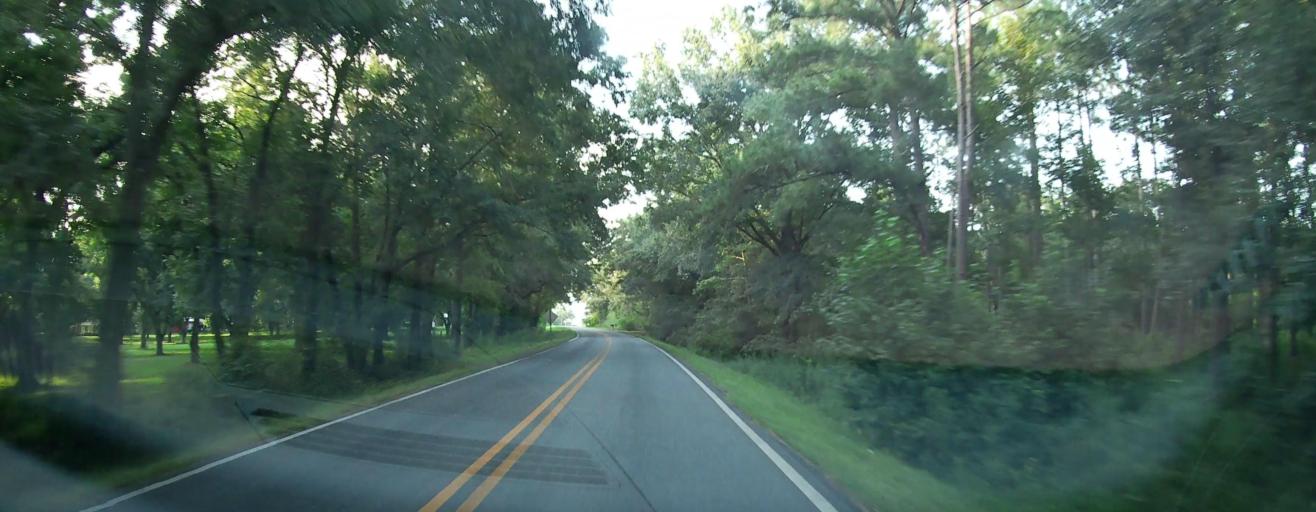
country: US
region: Georgia
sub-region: Pulaski County
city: Hawkinsville
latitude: 32.2690
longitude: -83.5380
